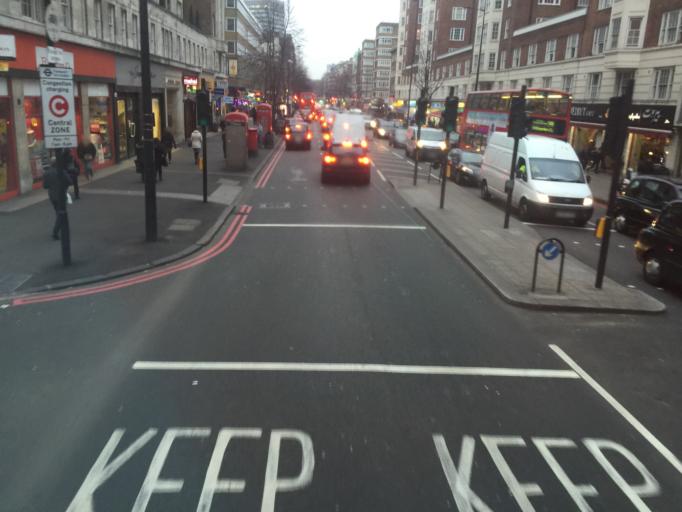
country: GB
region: England
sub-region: Greater London
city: Bayswater
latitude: 51.5169
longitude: -0.1656
